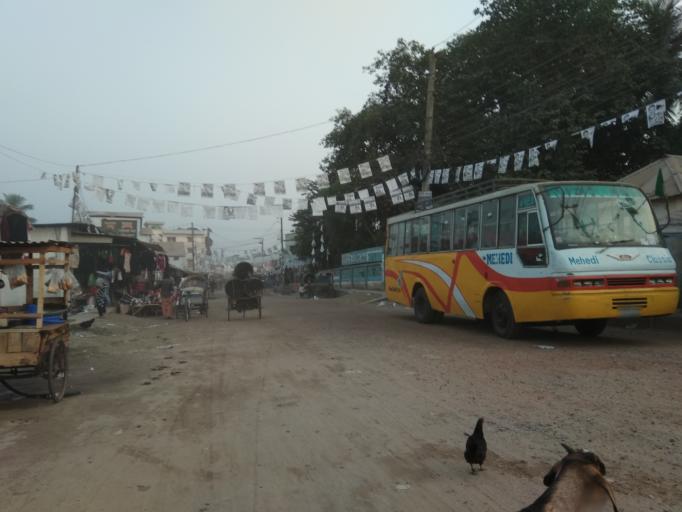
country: BD
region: Rangpur Division
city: Rangpur
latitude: 25.7318
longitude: 89.2639
